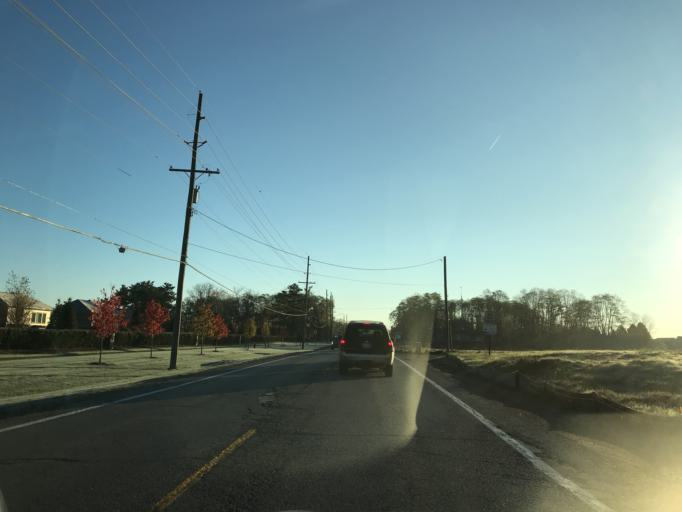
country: US
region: Michigan
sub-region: Oakland County
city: Novi
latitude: 42.4653
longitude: -83.5172
